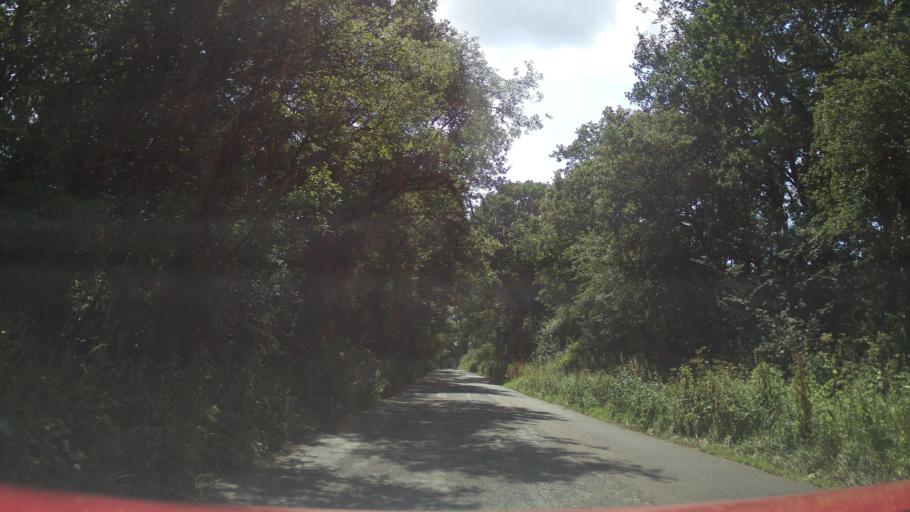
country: GB
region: England
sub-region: Wiltshire
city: Minety
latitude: 51.5928
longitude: -1.9361
